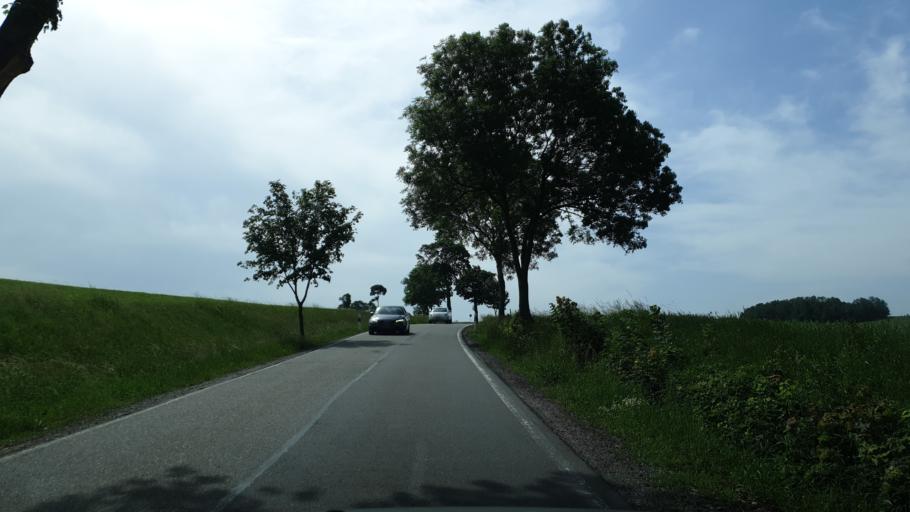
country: DE
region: Saxony
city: Zschorlau
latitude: 50.5584
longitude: 12.6464
